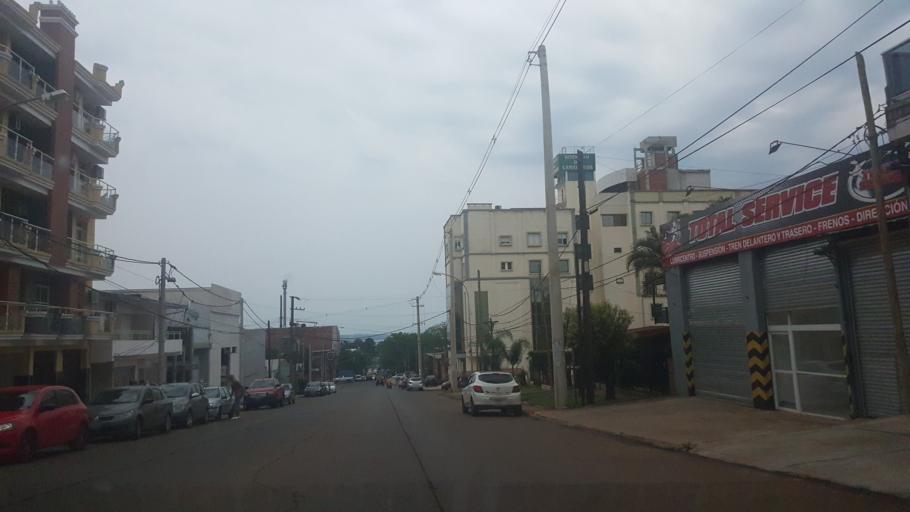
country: AR
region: Misiones
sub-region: Departamento de Capital
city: Posadas
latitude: -27.3933
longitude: -55.9105
